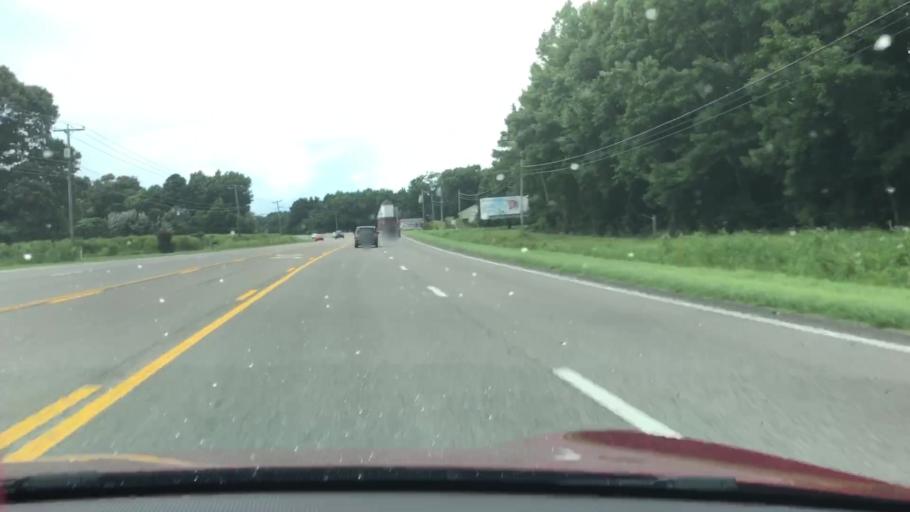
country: US
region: North Carolina
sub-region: Dare County
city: Southern Shores
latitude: 36.1305
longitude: -75.8378
